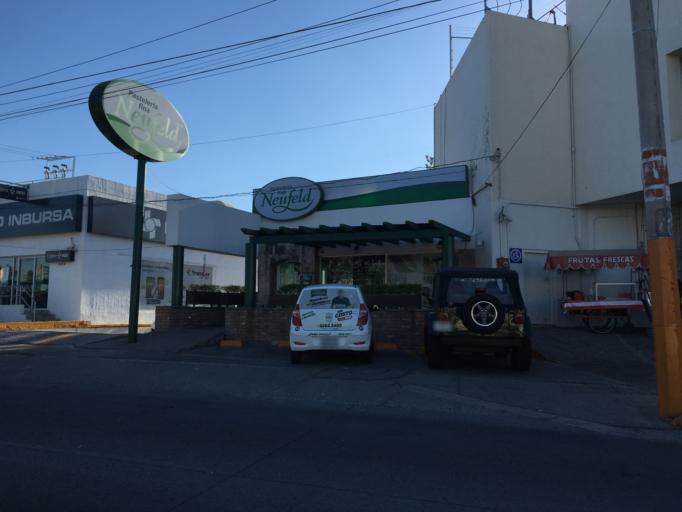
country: MX
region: Jalisco
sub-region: Zapopan
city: Zapopan
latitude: 20.7054
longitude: -103.3481
